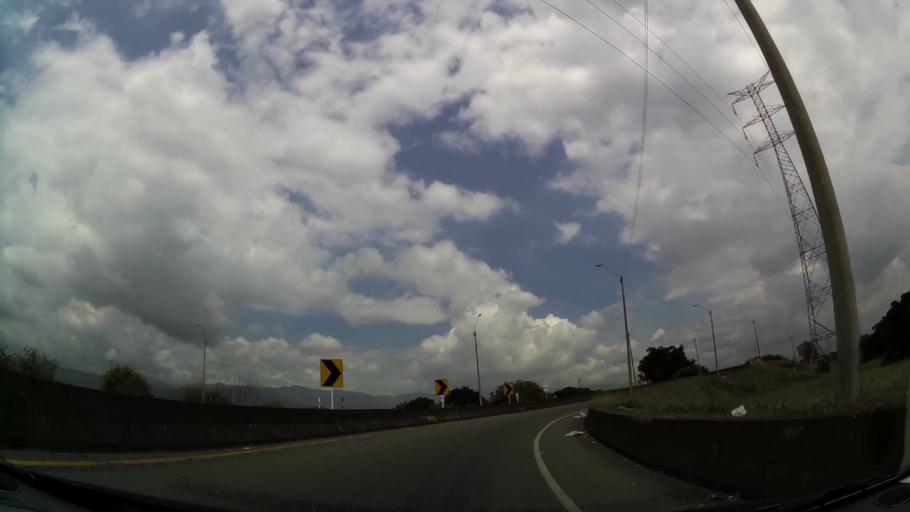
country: CO
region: Valle del Cauca
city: Cali
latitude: 3.4926
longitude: -76.4697
